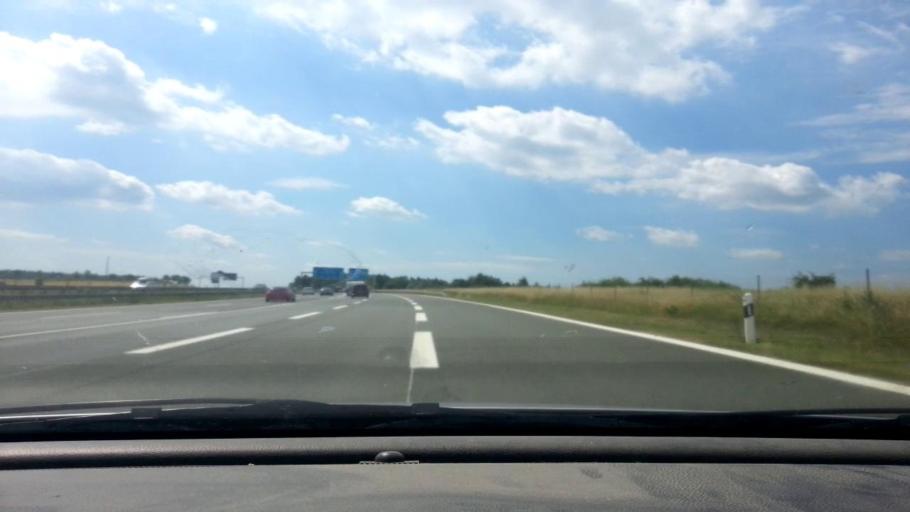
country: DE
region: Bavaria
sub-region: Upper Franconia
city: Harsdorf
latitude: 50.0204
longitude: 11.6040
